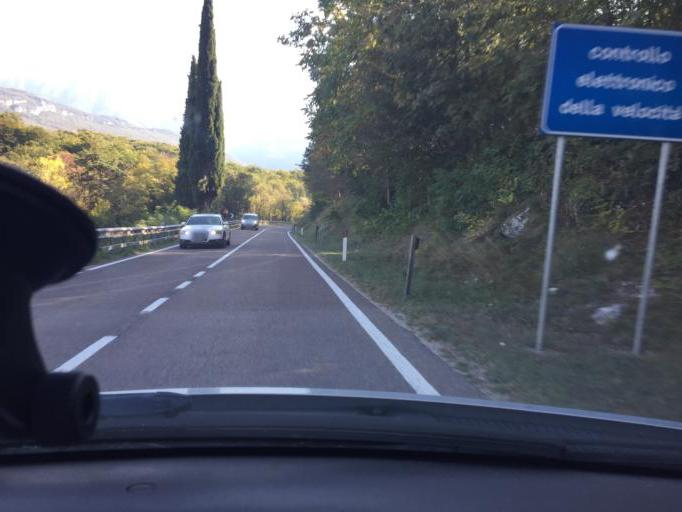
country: IT
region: Trentino-Alto Adige
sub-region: Provincia di Trento
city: Pietramurata
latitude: 46.0071
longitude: 10.9335
